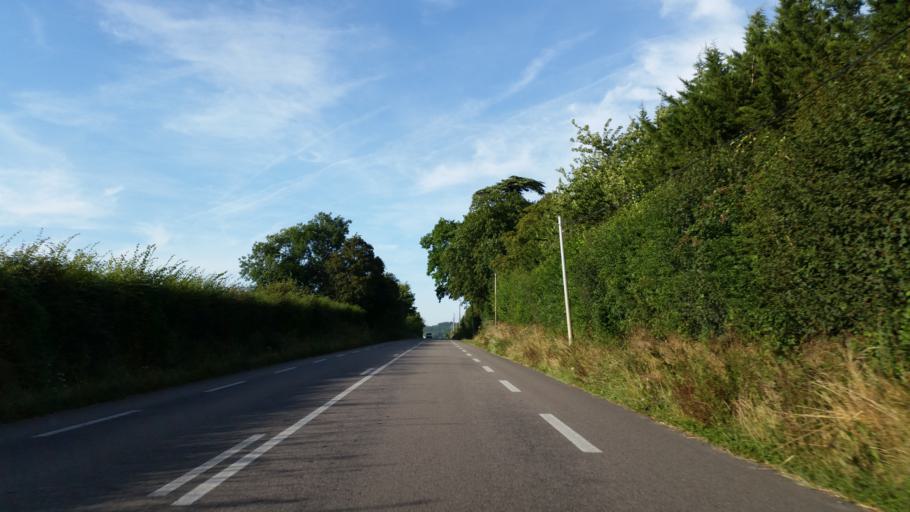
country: FR
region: Lower Normandy
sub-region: Departement du Calvados
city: Cambremer
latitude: 49.1051
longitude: 0.0049
